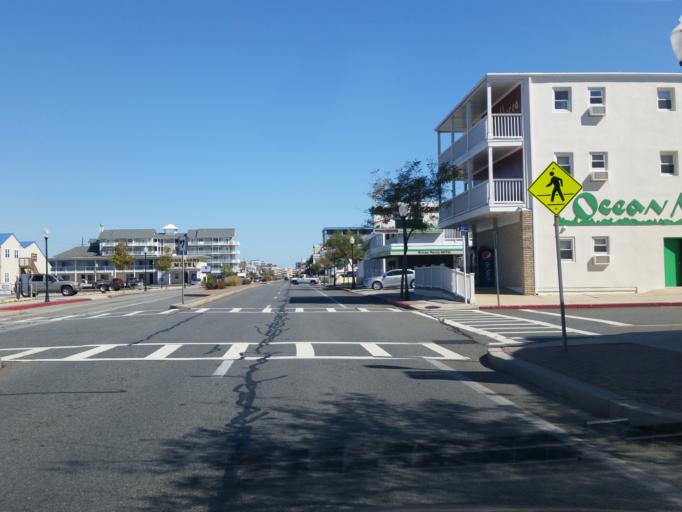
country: US
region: Maryland
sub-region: Worcester County
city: Ocean City
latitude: 38.3520
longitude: -75.0760
